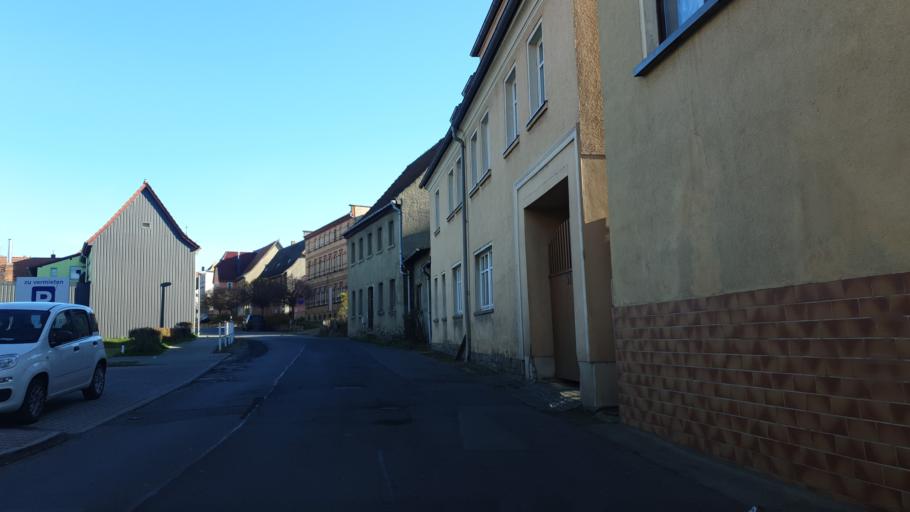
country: DE
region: Saxony-Anhalt
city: Droyssig
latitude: 51.0415
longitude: 12.0257
